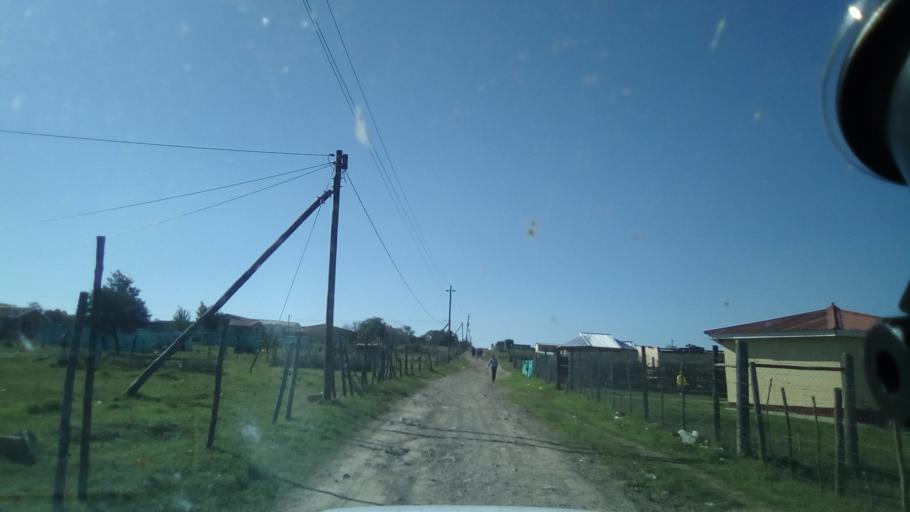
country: ZA
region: Eastern Cape
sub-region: Buffalo City Metropolitan Municipality
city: Bhisho
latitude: -32.8287
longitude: 27.3692
